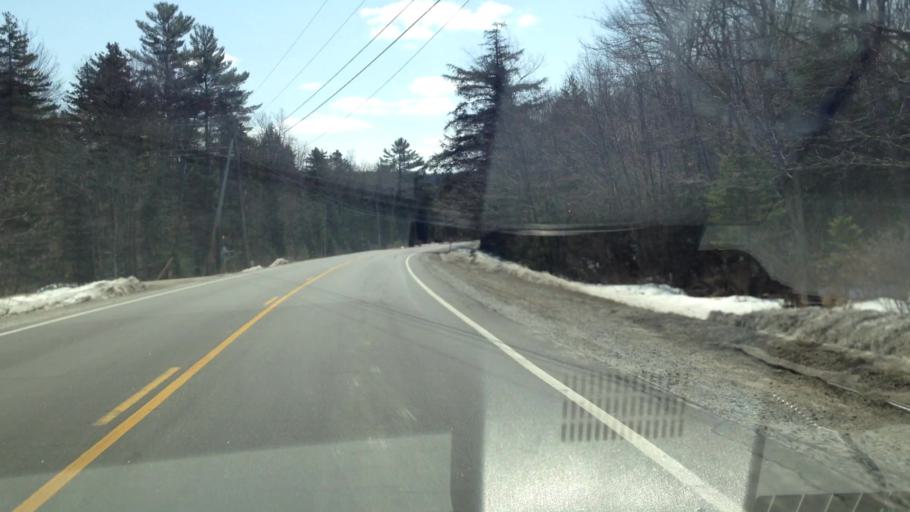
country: US
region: New Hampshire
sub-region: Merrimack County
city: Wilmot
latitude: 43.4701
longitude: -71.9613
